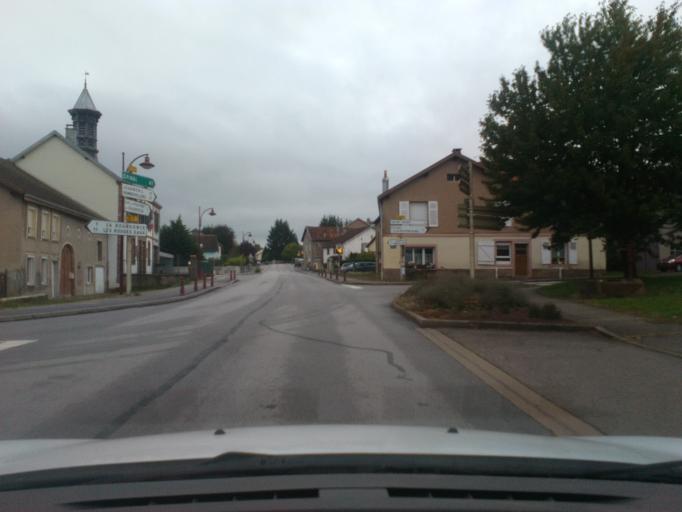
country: FR
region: Lorraine
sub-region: Departement des Vosges
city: Etival-Clairefontaine
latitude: 48.3230
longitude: 6.8275
